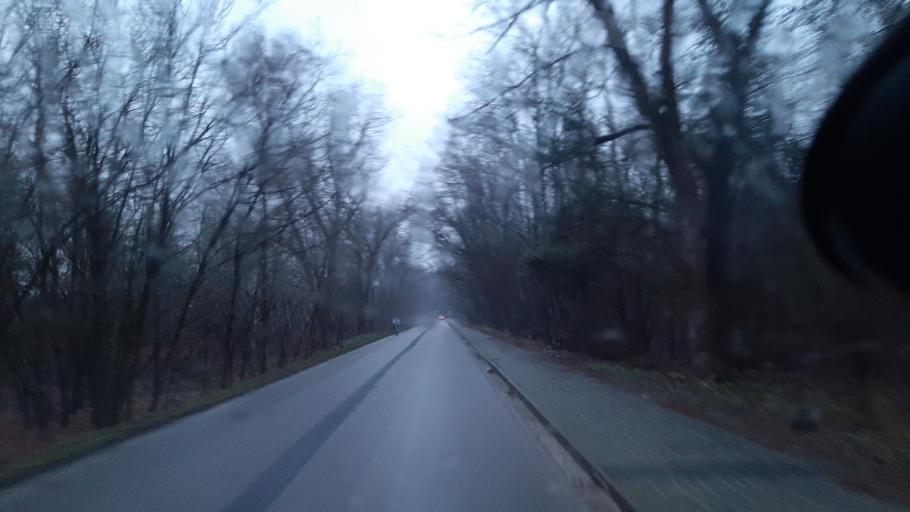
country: PL
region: Lublin Voivodeship
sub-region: Powiat lubartowski
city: Firlej
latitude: 51.5579
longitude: 22.5293
